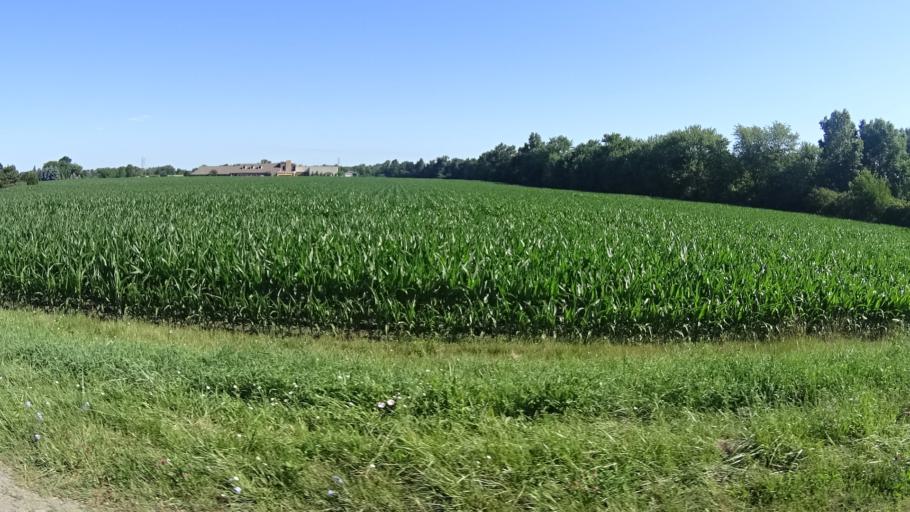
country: US
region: Ohio
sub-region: Erie County
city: Sandusky
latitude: 41.3961
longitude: -82.6430
